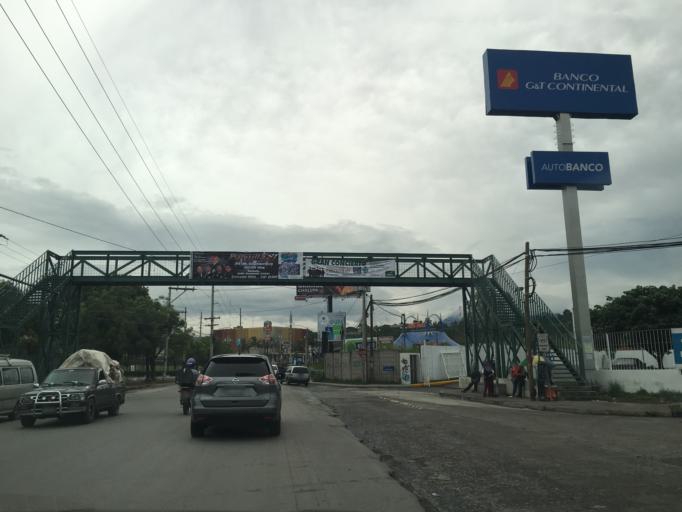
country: GT
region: Guatemala
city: Petapa
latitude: 14.5242
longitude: -90.5618
